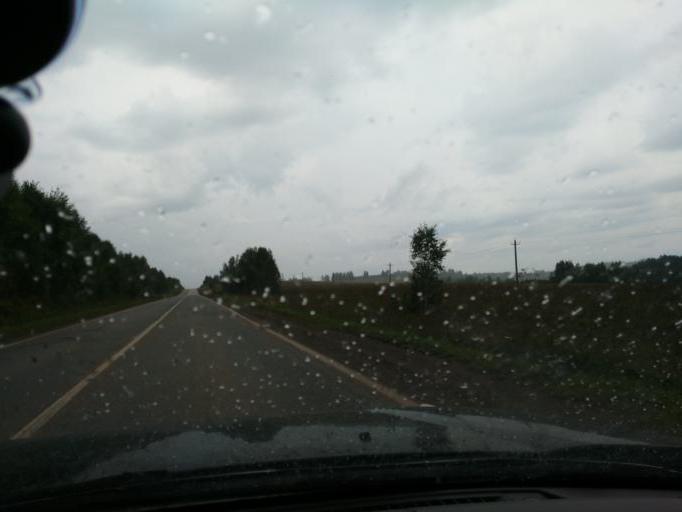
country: RU
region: Perm
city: Barda
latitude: 56.8652
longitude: 55.9024
